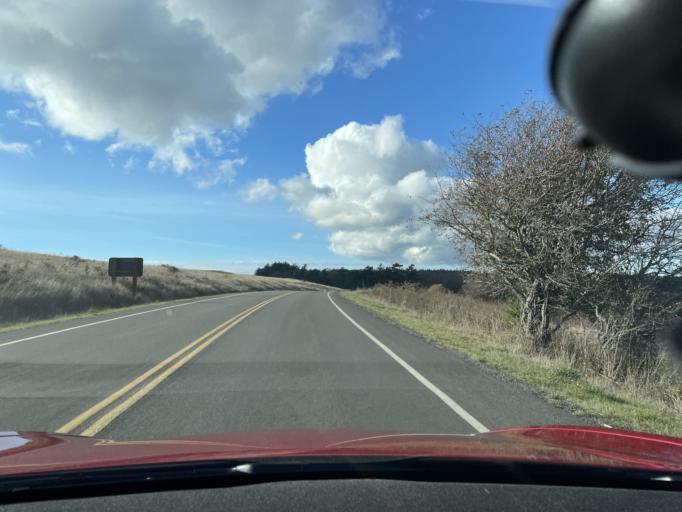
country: US
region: Washington
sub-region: San Juan County
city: Friday Harbor
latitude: 48.4640
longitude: -123.0025
